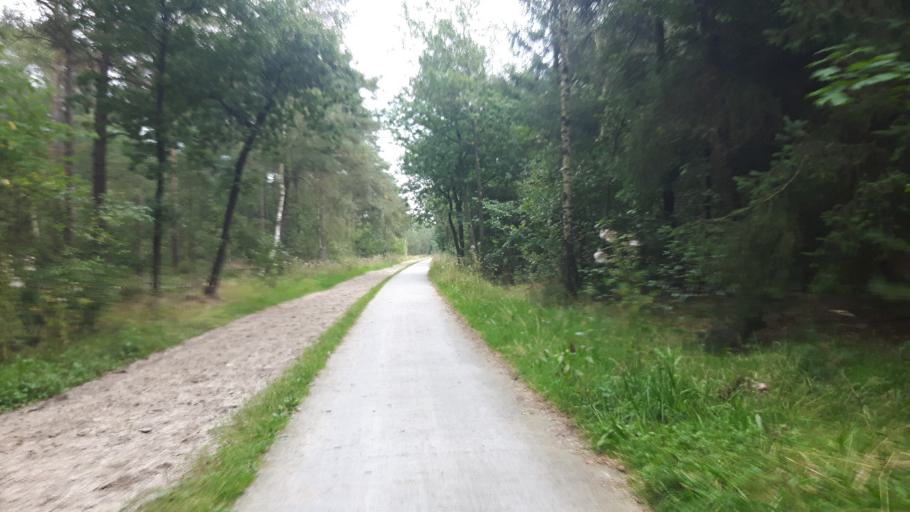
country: NL
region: Drenthe
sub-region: Gemeente Westerveld
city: Dwingeloo
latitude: 52.9461
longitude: 6.2959
